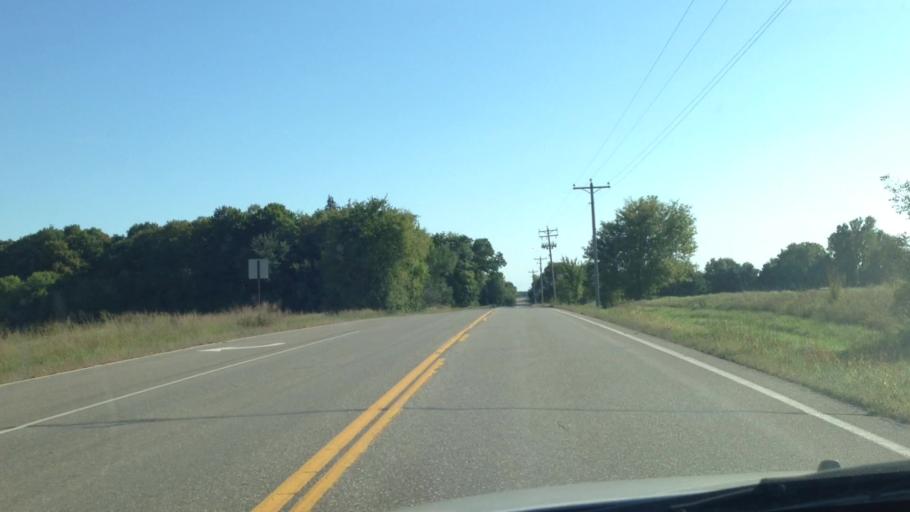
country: US
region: Minnesota
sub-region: Washington County
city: Stillwater
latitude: 45.0966
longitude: -92.8128
